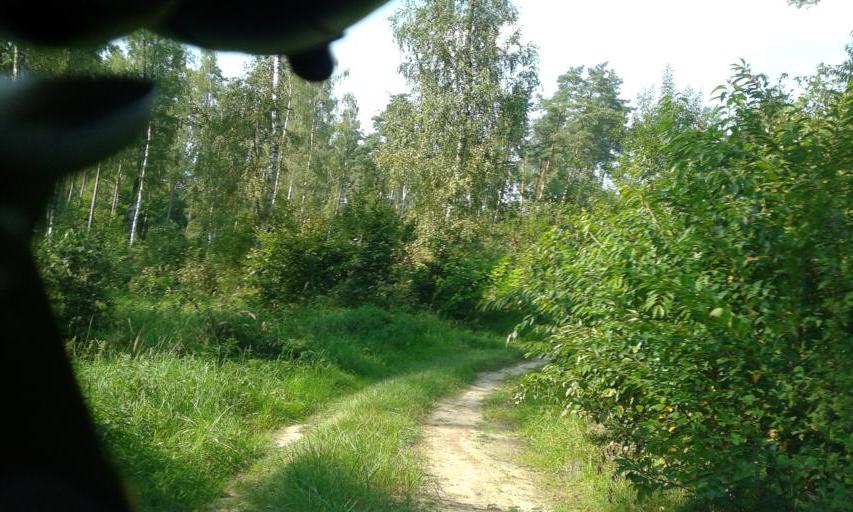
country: PL
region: West Pomeranian Voivodeship
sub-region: Powiat choszczenski
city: Krzecin
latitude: 53.0851
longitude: 15.4599
